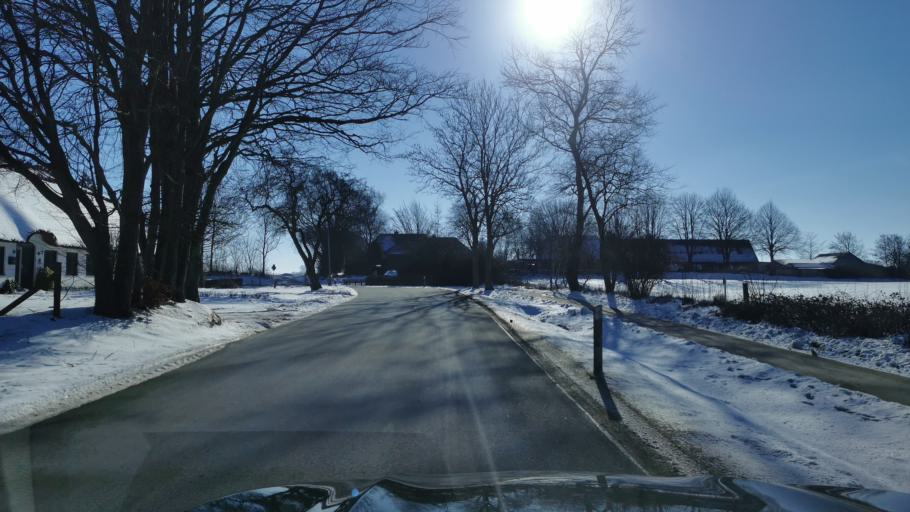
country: DE
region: Schleswig-Holstein
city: Sorup
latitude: 54.7333
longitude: 9.6484
